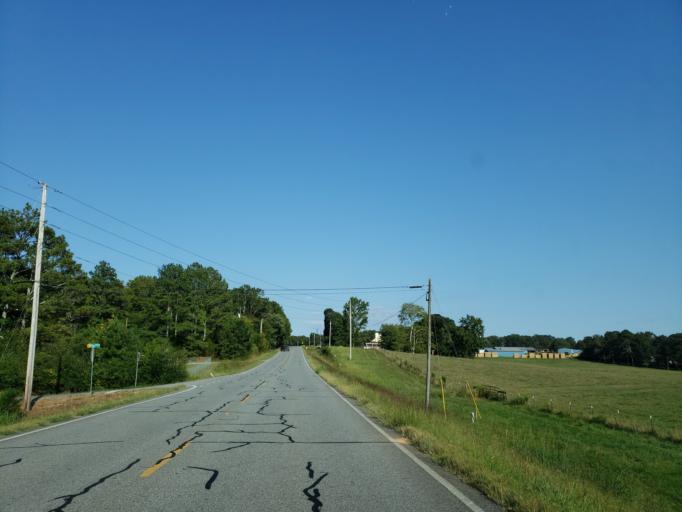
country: US
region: Georgia
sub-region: Whitfield County
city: Varnell
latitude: 34.9063
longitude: -84.8879
